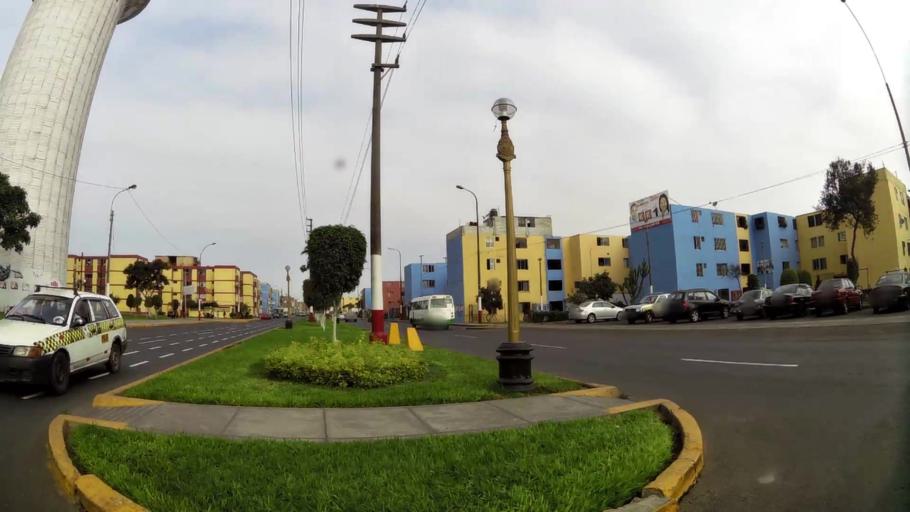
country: PE
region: Callao
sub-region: Callao
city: Callao
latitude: -12.0138
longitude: -77.1000
